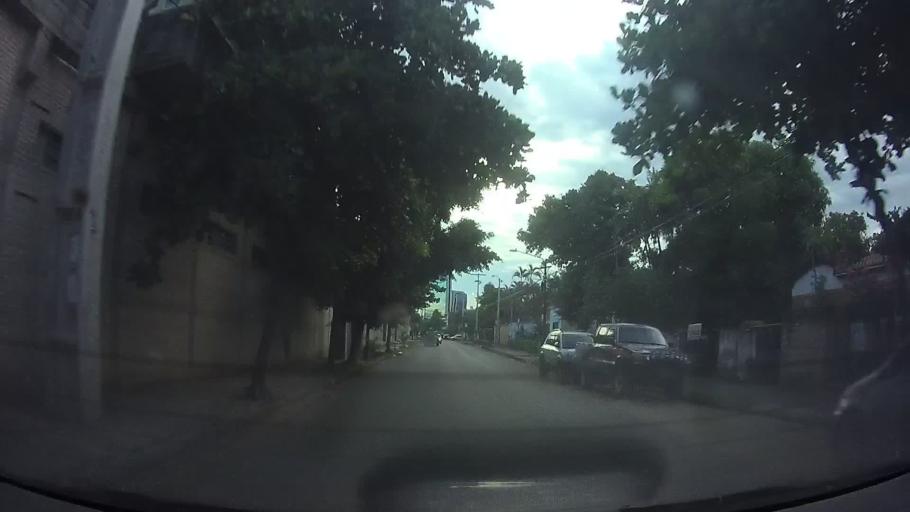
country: PY
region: Central
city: Fernando de la Mora
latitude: -25.2754
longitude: -57.5520
